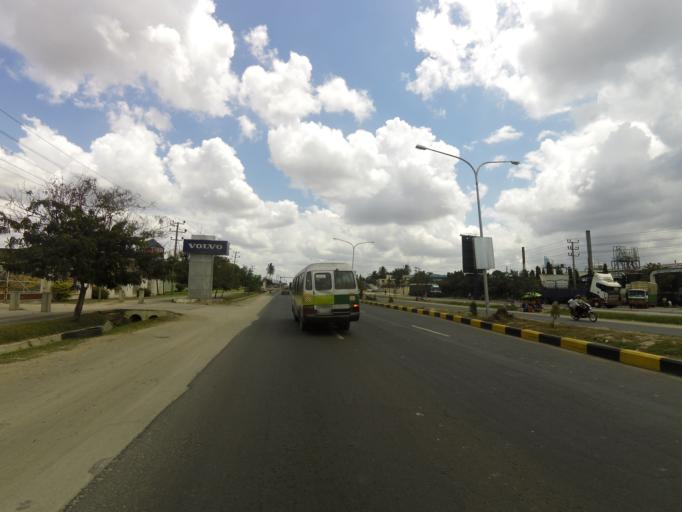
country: TZ
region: Dar es Salaam
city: Dar es Salaam
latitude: -6.8573
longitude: 39.2192
